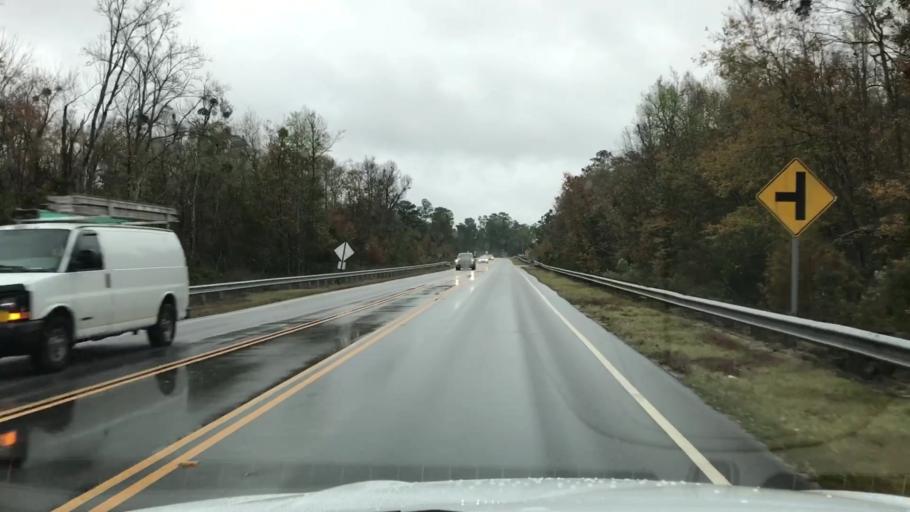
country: US
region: South Carolina
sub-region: Horry County
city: Forestbrook
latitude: 33.7588
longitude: -78.9173
